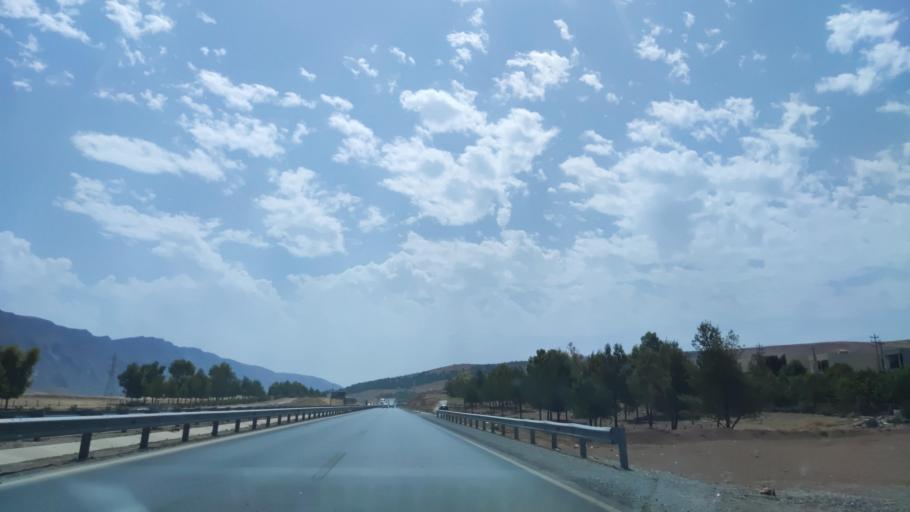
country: IQ
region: Arbil
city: Shaqlawah
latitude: 36.5029
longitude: 44.3550
